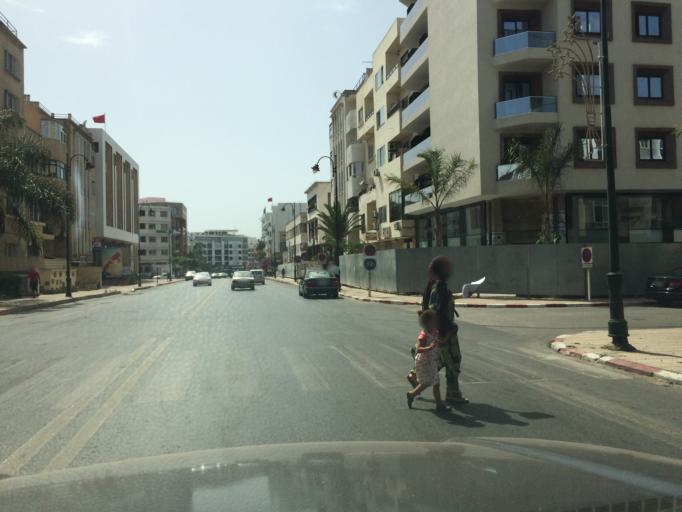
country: MA
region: Rabat-Sale-Zemmour-Zaer
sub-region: Rabat
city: Rabat
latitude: 34.0173
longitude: -6.8251
